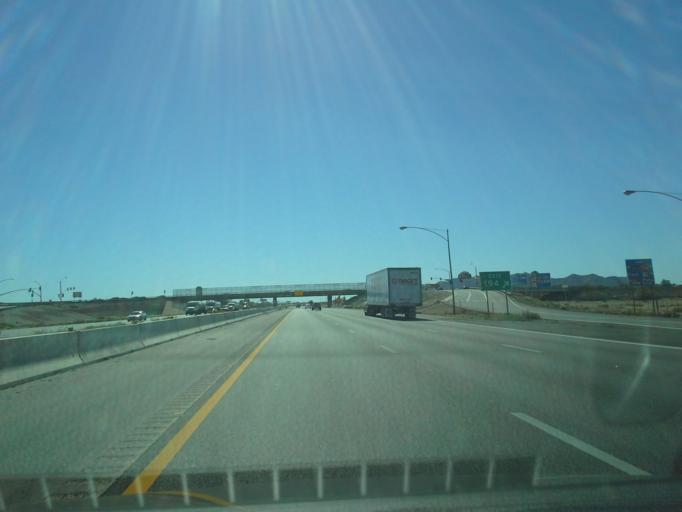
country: US
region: Arizona
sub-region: Pinal County
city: Casa Grande
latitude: 32.8824
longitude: -111.6870
